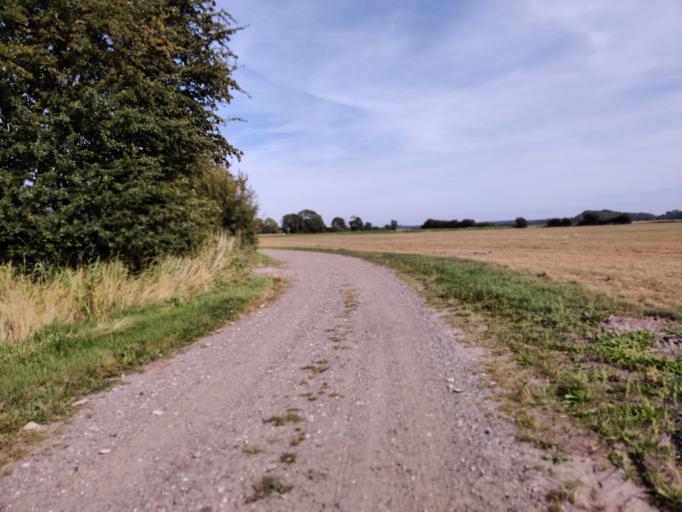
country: DK
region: Zealand
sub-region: Guldborgsund Kommune
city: Nykobing Falster
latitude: 54.6435
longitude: 11.9122
